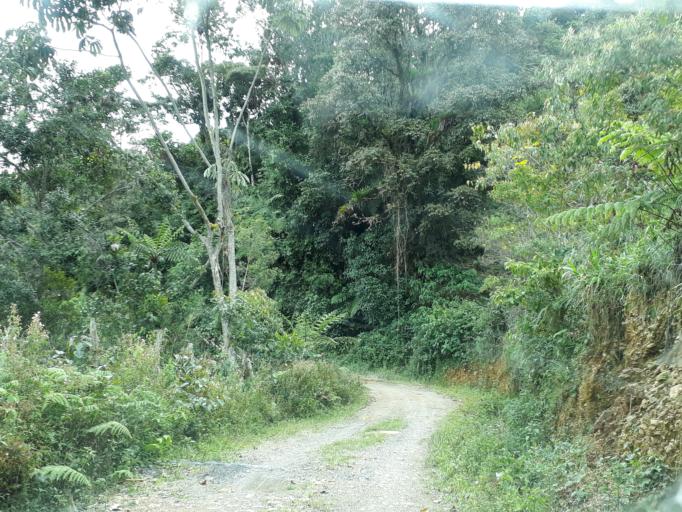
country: CO
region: Boyaca
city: Quipama
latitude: 5.3941
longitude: -74.1144
